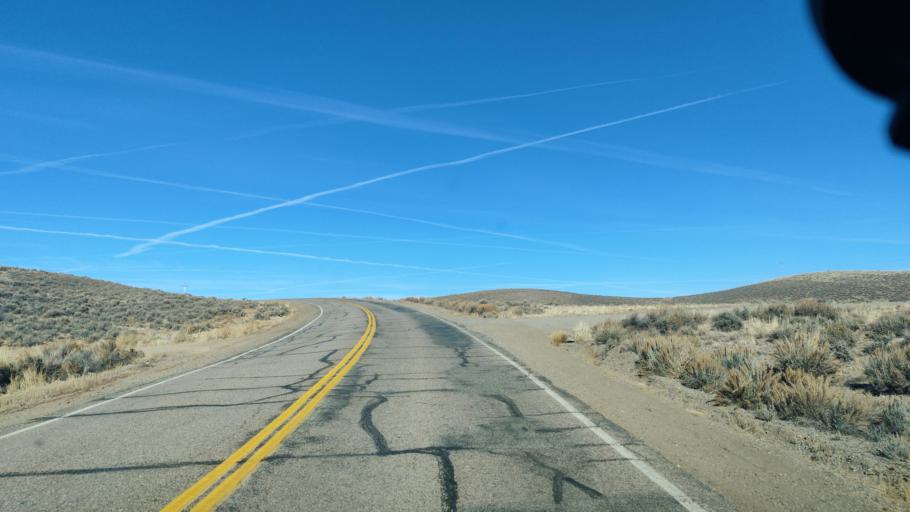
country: US
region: Colorado
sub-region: Gunnison County
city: Gunnison
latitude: 38.5350
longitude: -106.9579
